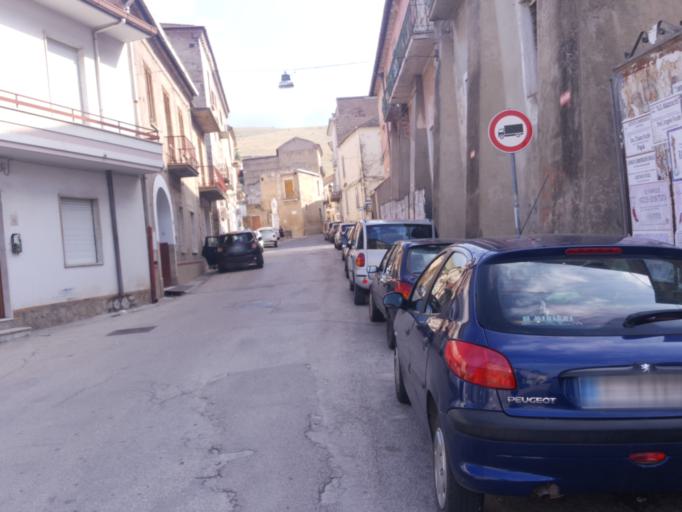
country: IT
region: Campania
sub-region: Provincia di Caserta
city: Pignataro Maggiore
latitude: 41.1897
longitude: 14.1702
